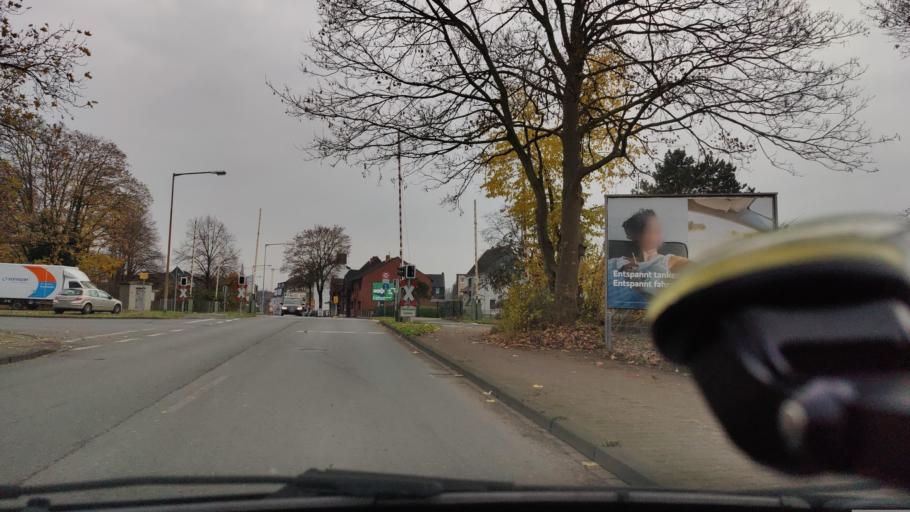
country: DE
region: North Rhine-Westphalia
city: Lunen
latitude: 51.6254
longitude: 7.5122
